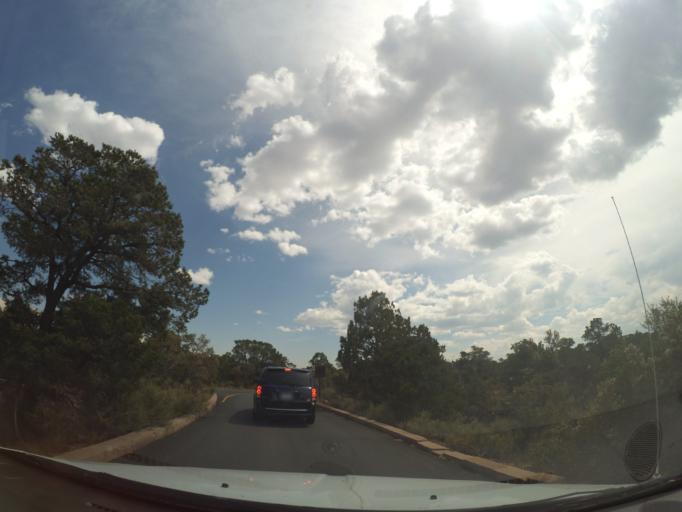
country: US
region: Arizona
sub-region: Coconino County
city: Grand Canyon
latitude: 36.0042
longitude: -111.9243
